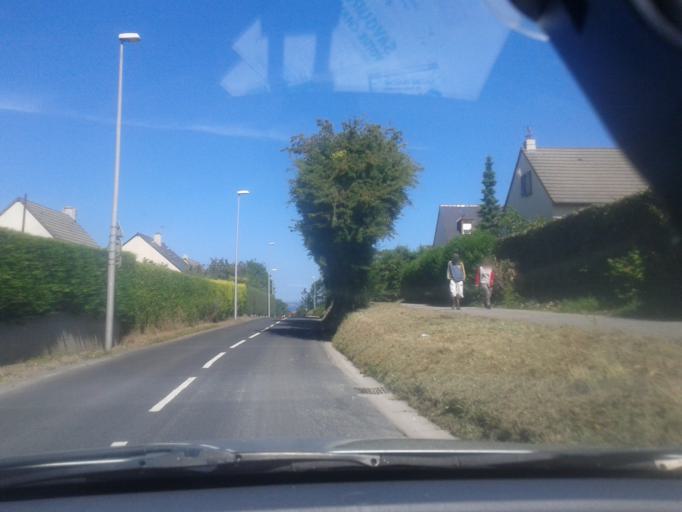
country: FR
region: Lower Normandy
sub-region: Departement de la Manche
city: Equeurdreville-Hainneville
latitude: 49.6527
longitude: -1.6656
